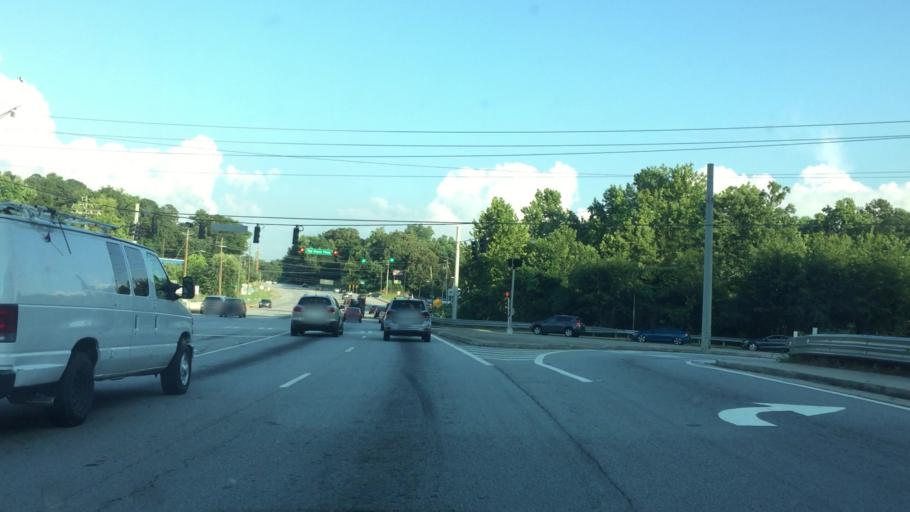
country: US
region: Georgia
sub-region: DeKalb County
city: Panthersville
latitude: 33.6870
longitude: -84.2025
